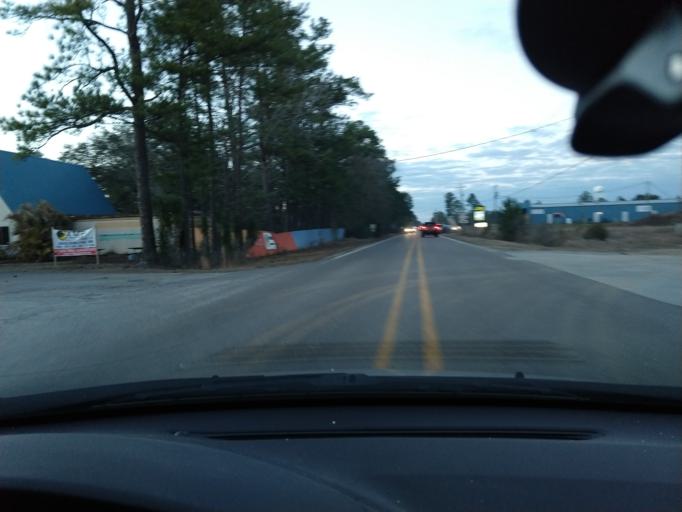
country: US
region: Mississippi
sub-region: Jackson County
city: Gulf Park Estates
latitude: 30.4470
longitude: -88.7181
